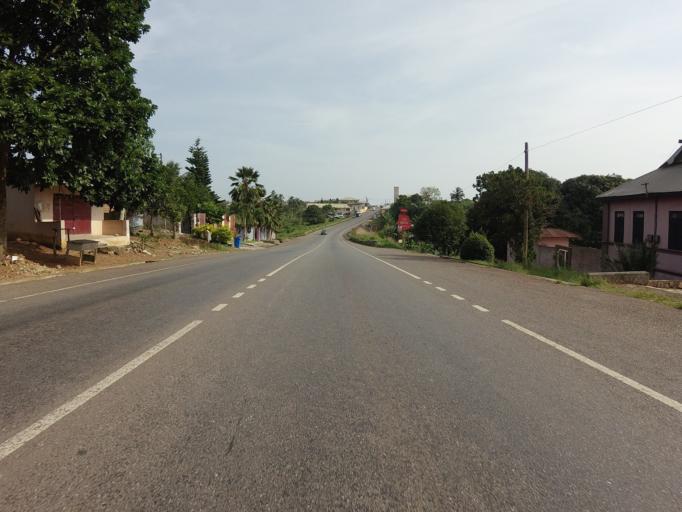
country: GH
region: Eastern
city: Aburi
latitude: 5.8871
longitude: -0.1553
